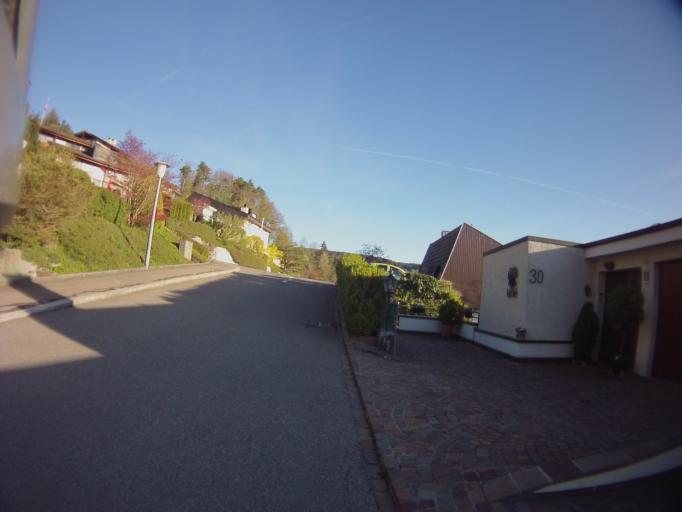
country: CH
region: Zurich
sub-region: Bezirk Dietikon
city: Birmensdorf
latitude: 47.3489
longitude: 8.4447
